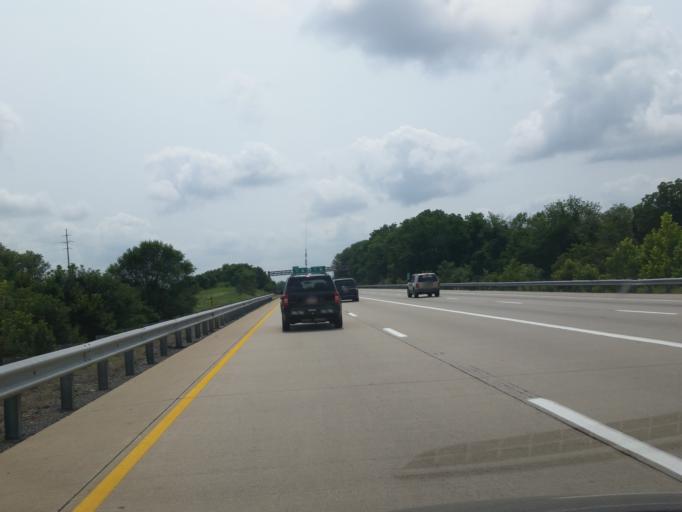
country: US
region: Pennsylvania
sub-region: Dauphin County
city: Colonial Park
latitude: 40.3169
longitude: -76.8261
